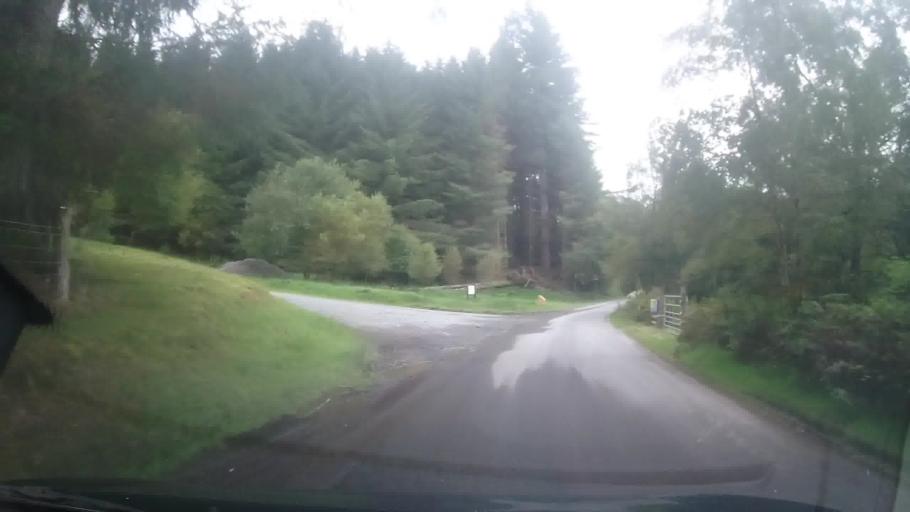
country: GB
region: Wales
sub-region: Sir Powys
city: Rhayader
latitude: 52.2918
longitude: -3.6113
